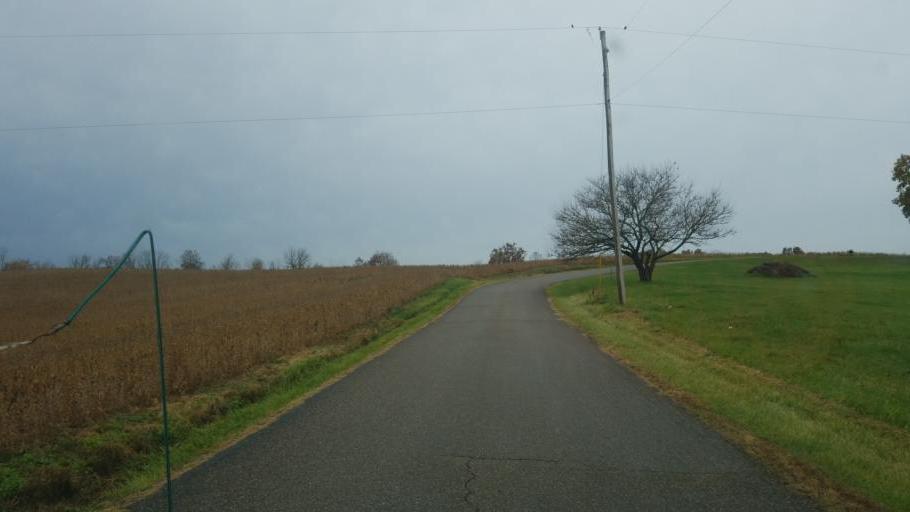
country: US
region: Ohio
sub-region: Washington County
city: Beverly
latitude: 39.5513
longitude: -81.7033
